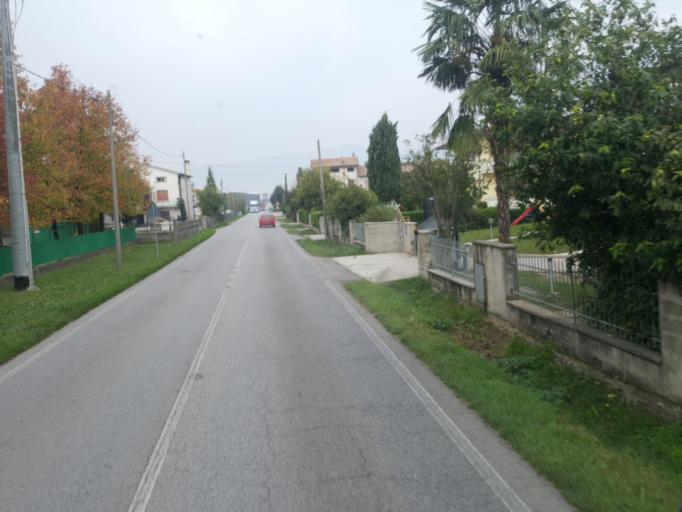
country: IT
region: Veneto
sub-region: Provincia di Treviso
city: Ramon
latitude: 45.7034
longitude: 11.8728
